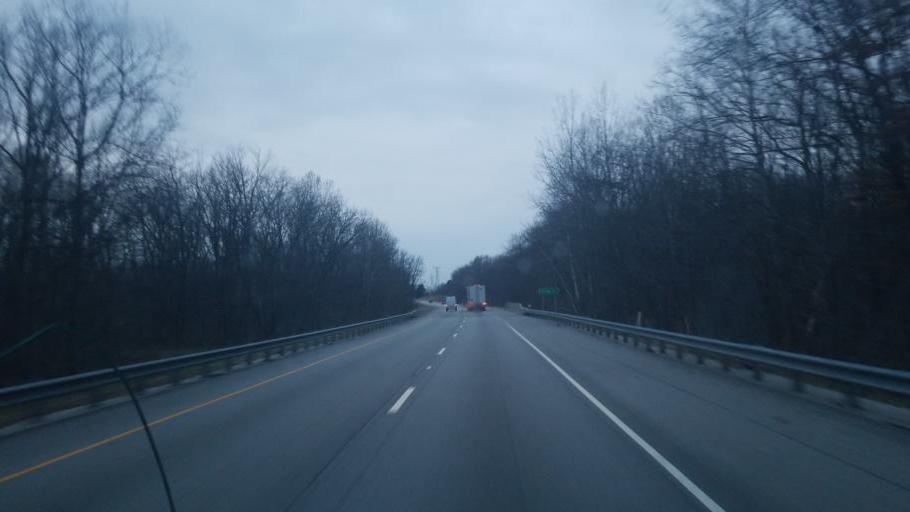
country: US
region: Indiana
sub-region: Vigo County
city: Seelyville
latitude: 39.4442
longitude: -87.2672
